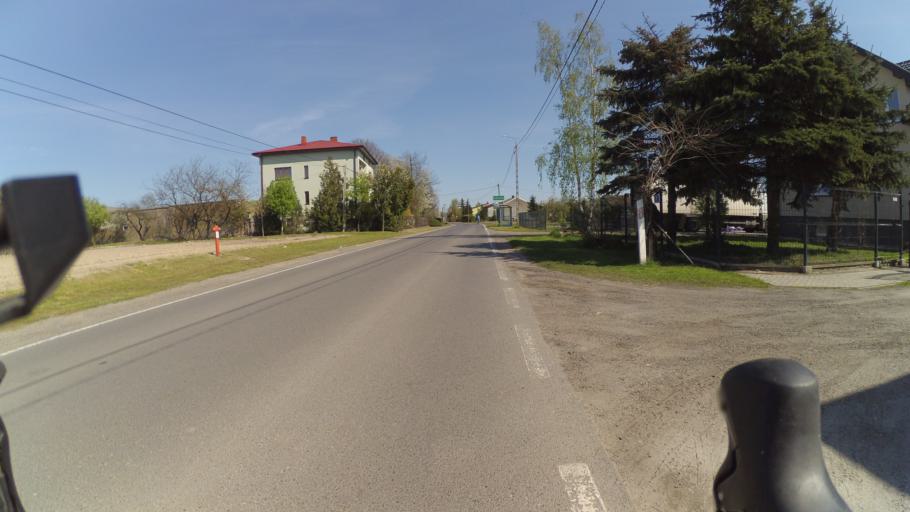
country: PL
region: Masovian Voivodeship
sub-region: Powiat warszawski zachodni
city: Leszno
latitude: 52.2445
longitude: 20.5457
